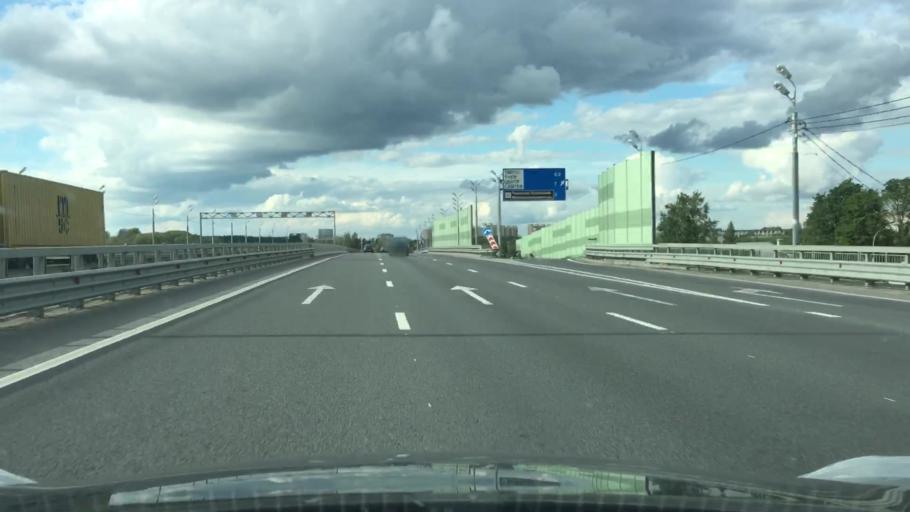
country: RU
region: Tverskaya
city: Tver
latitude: 56.8322
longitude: 35.8025
